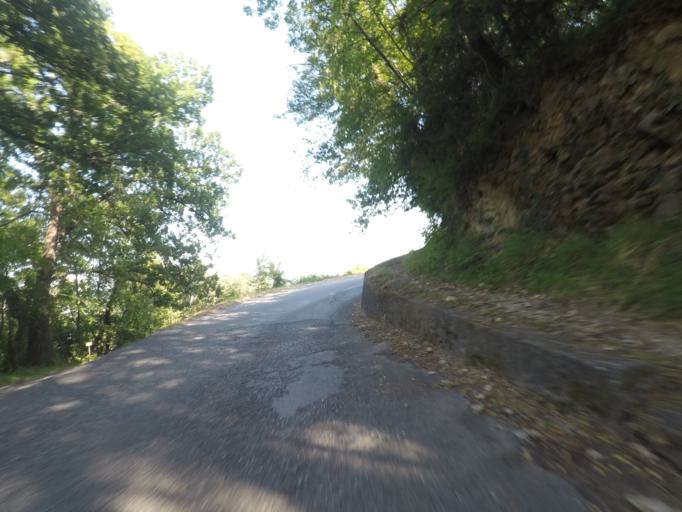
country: IT
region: Tuscany
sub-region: Provincia di Massa-Carrara
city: Carrara
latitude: 44.0729
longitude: 10.0693
